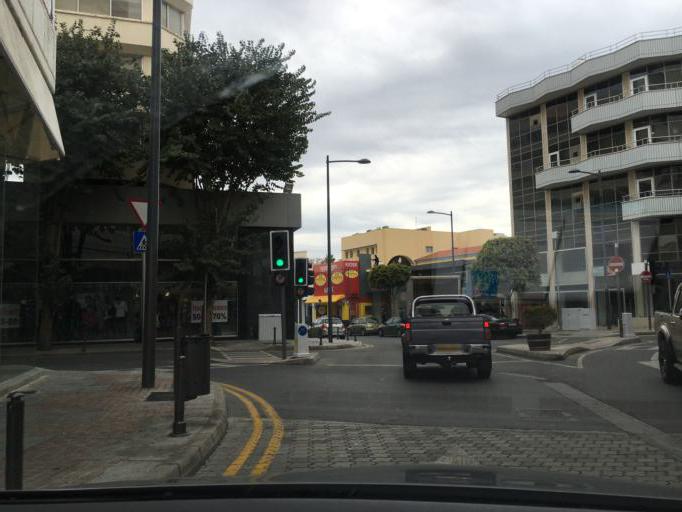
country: CY
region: Limassol
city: Limassol
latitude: 34.6767
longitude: 33.0453
